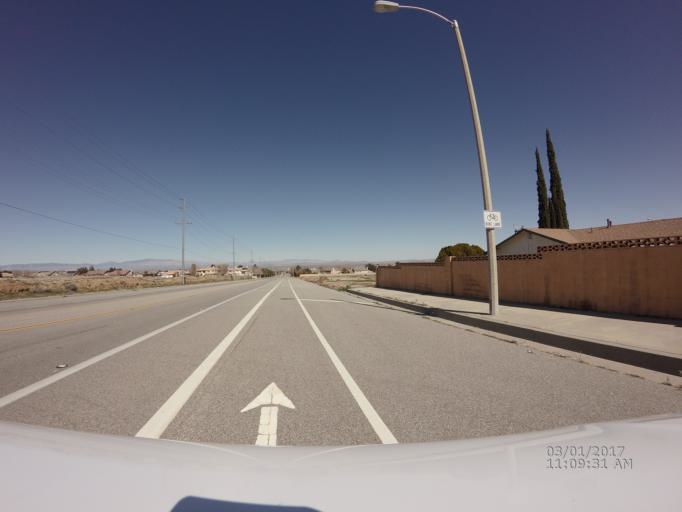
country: US
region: California
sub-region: Los Angeles County
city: Quartz Hill
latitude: 34.6473
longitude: -118.2536
